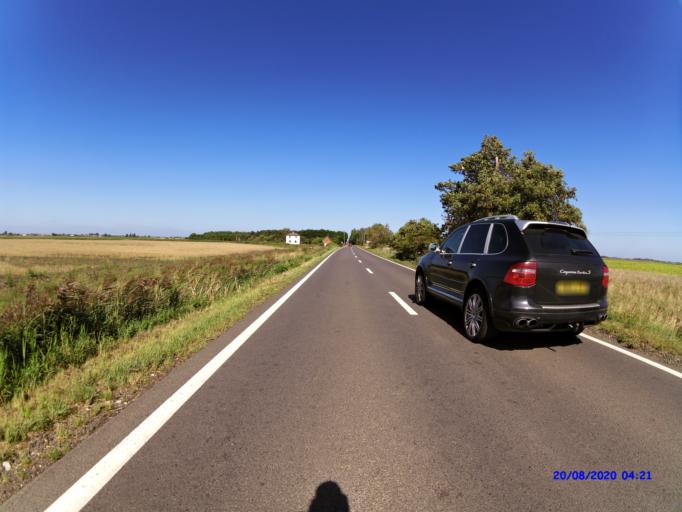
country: GB
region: England
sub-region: Cambridgeshire
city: Ramsey
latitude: 52.4956
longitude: -0.1229
